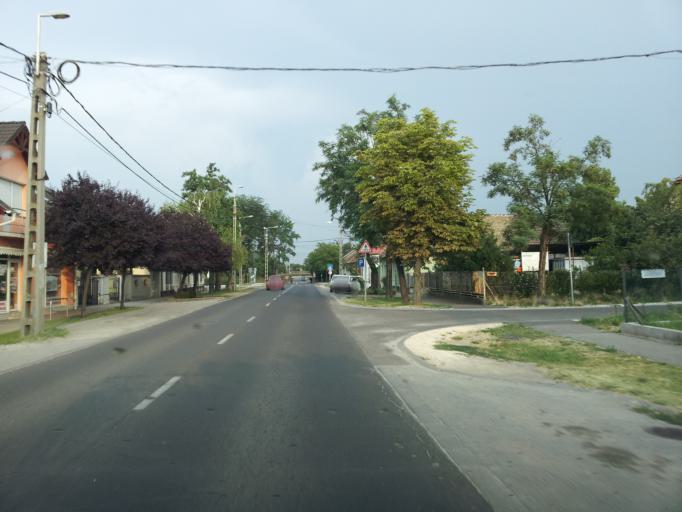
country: HU
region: Pest
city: Dunaharaszti
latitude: 47.3533
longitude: 19.0942
